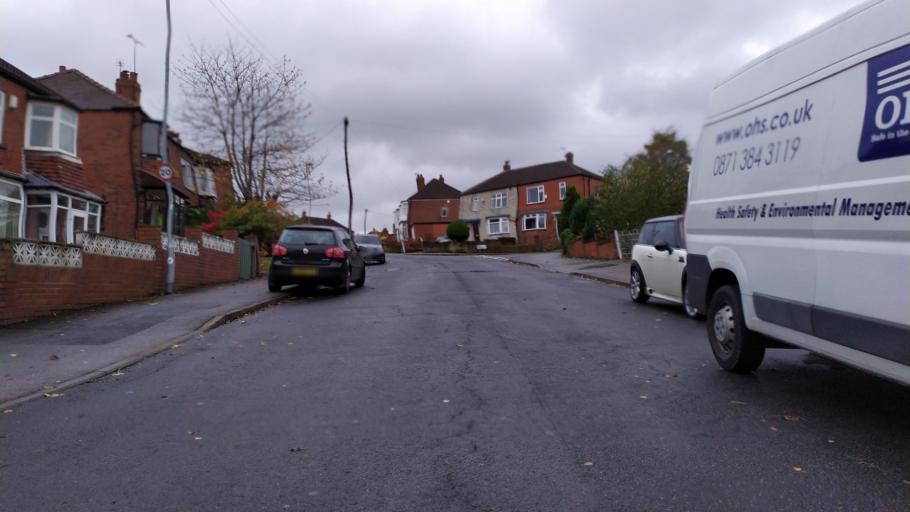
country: GB
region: England
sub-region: City and Borough of Leeds
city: Leeds
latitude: 53.8164
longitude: -1.5903
